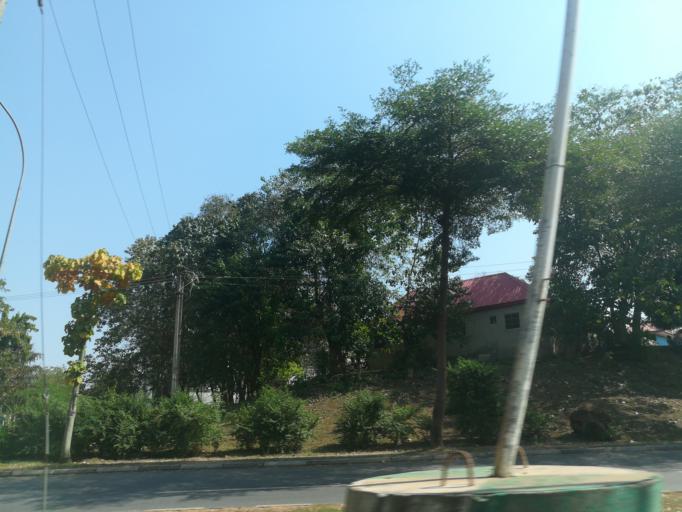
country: NG
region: Abuja Federal Capital Territory
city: Abuja
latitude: 9.0584
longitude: 7.4586
